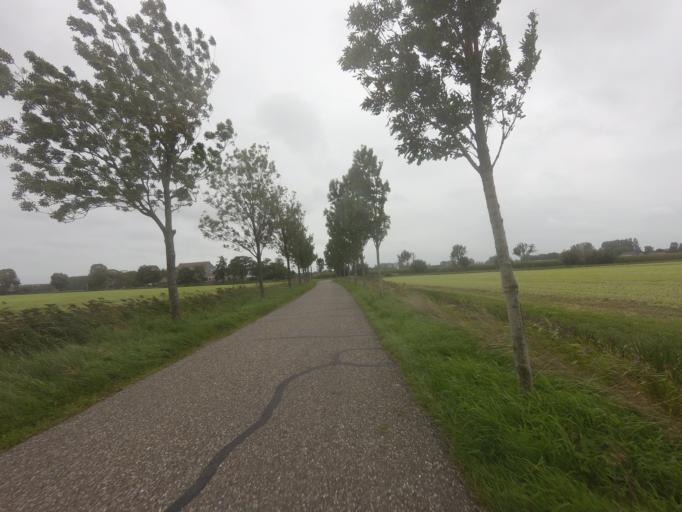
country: NL
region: Friesland
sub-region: Gemeente Leeuwarden
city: Bilgaard
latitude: 53.2291
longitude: 5.7817
